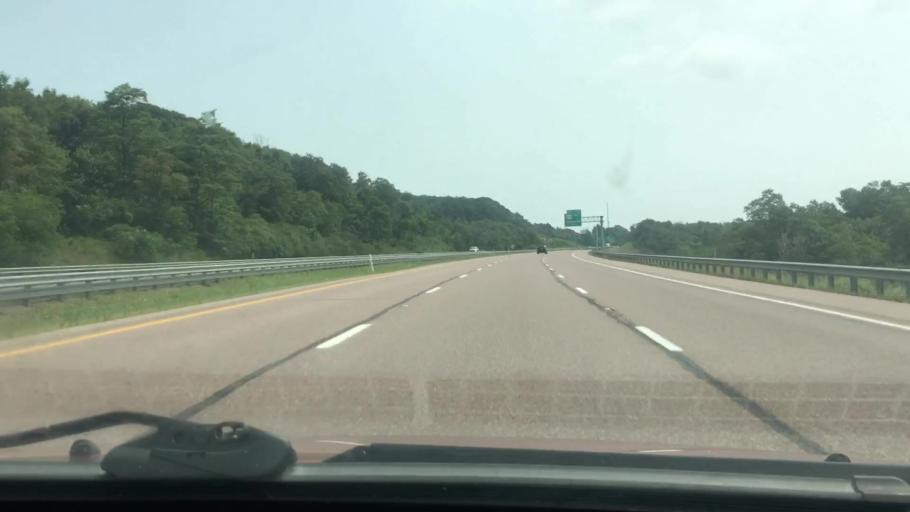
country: US
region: Pennsylvania
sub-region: Somerset County
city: Meyersdale
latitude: 39.6954
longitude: -79.2678
